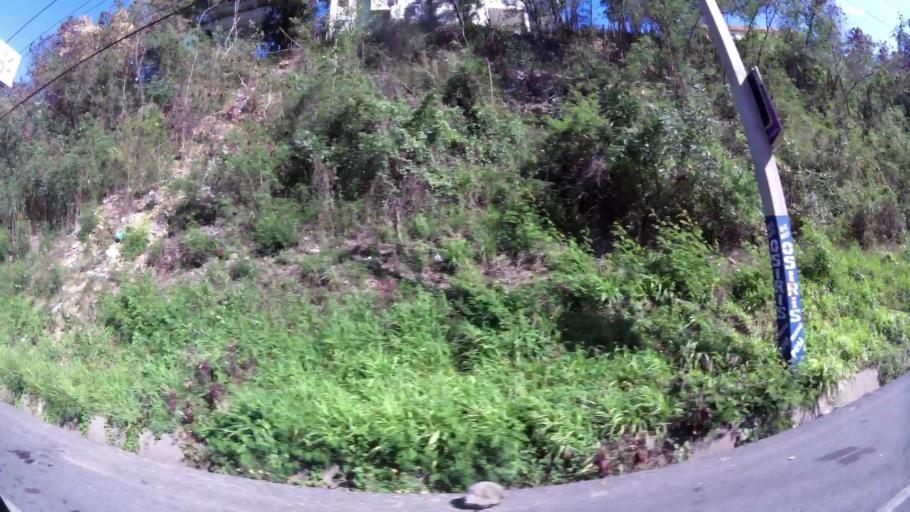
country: DO
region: San Cristobal
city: San Cristobal
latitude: 18.4326
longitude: -70.0894
